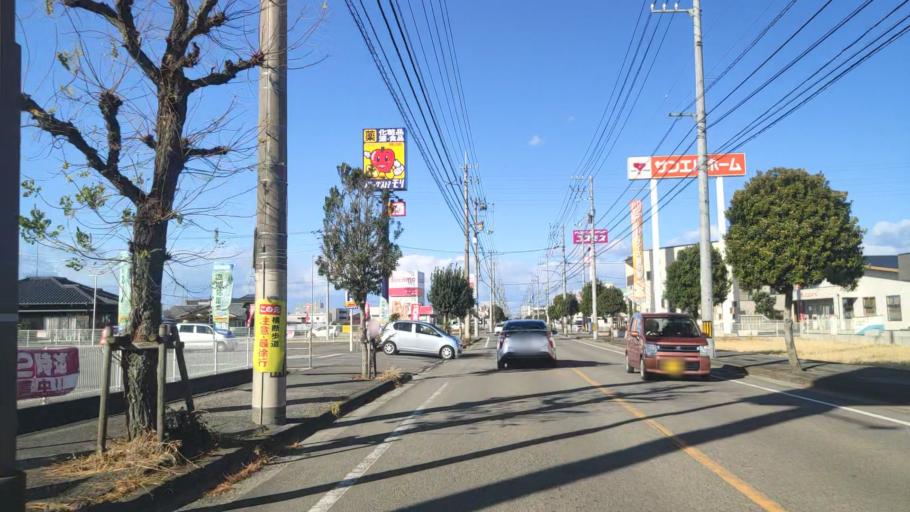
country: JP
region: Ehime
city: Saijo
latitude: 33.9247
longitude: 133.1911
